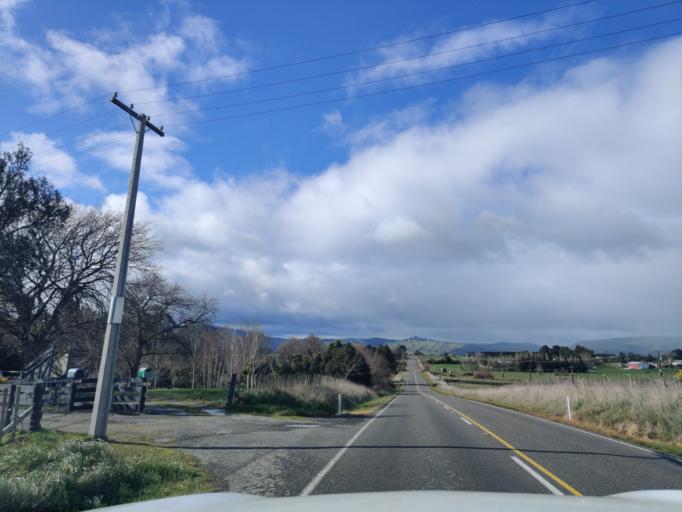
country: NZ
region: Manawatu-Wanganui
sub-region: Palmerston North City
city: Palmerston North
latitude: -40.2894
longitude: 175.7077
